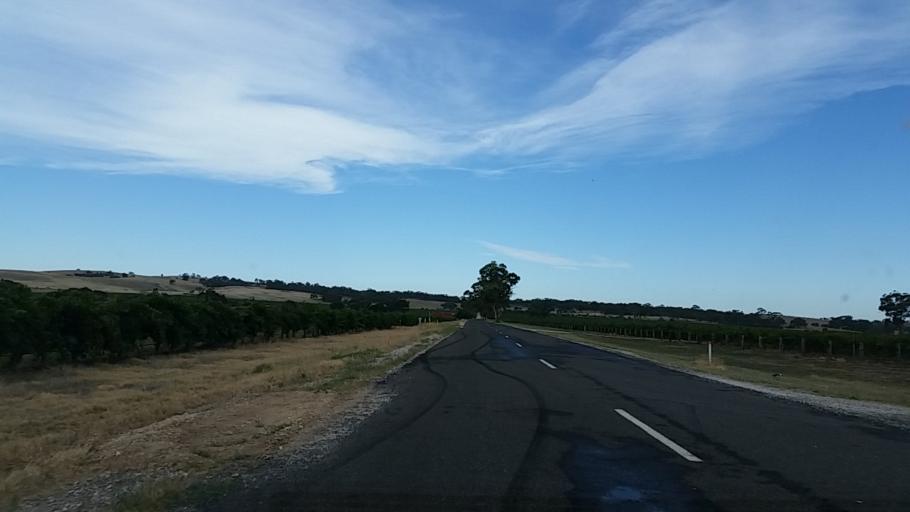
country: AU
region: South Australia
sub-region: Barossa
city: Nuriootpa
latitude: -34.4472
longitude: 139.0395
